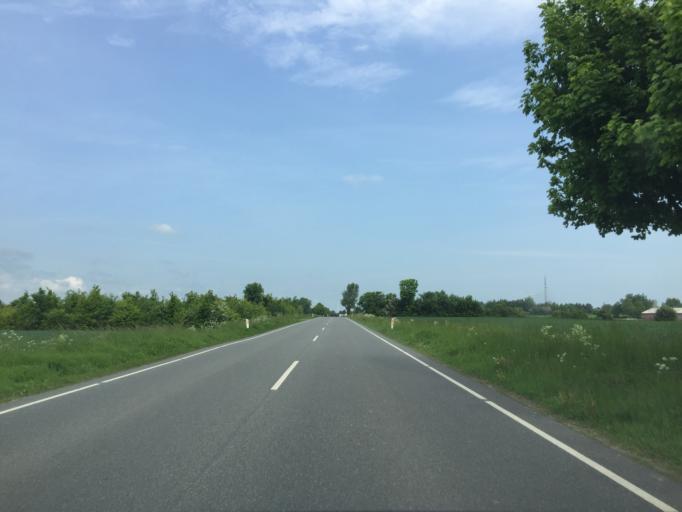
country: DK
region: South Denmark
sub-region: Nyborg Kommune
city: Nyborg
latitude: 55.1824
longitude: 10.7332
